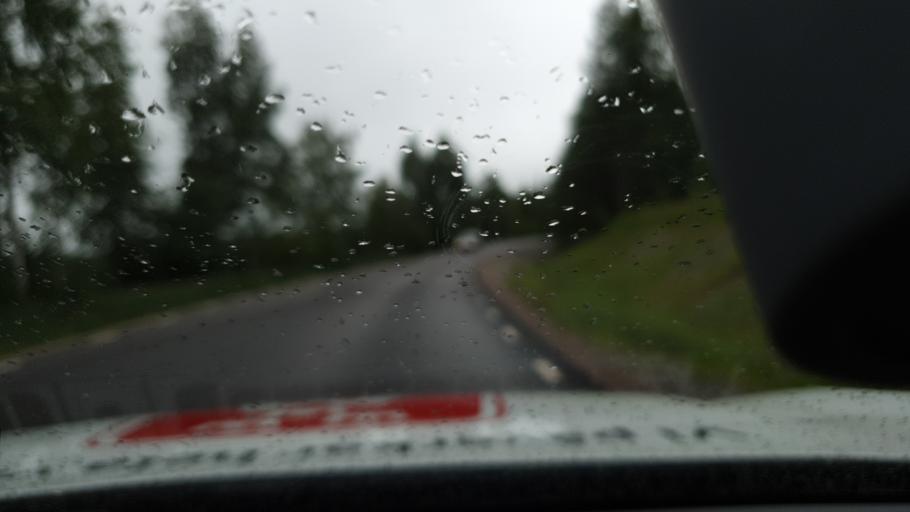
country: SE
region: Norrbotten
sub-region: Overtornea Kommun
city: OEvertornea
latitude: 66.4836
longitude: 23.4567
